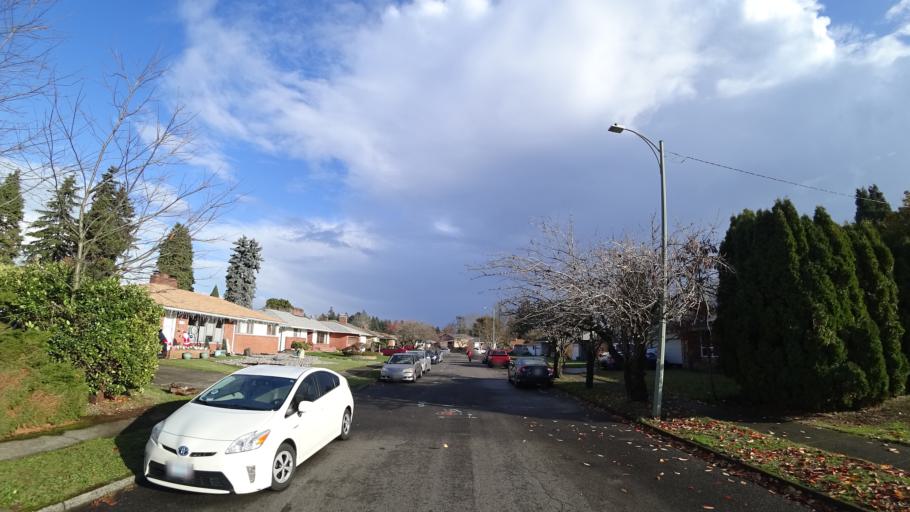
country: US
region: Oregon
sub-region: Multnomah County
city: Lents
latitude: 45.5272
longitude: -122.5556
